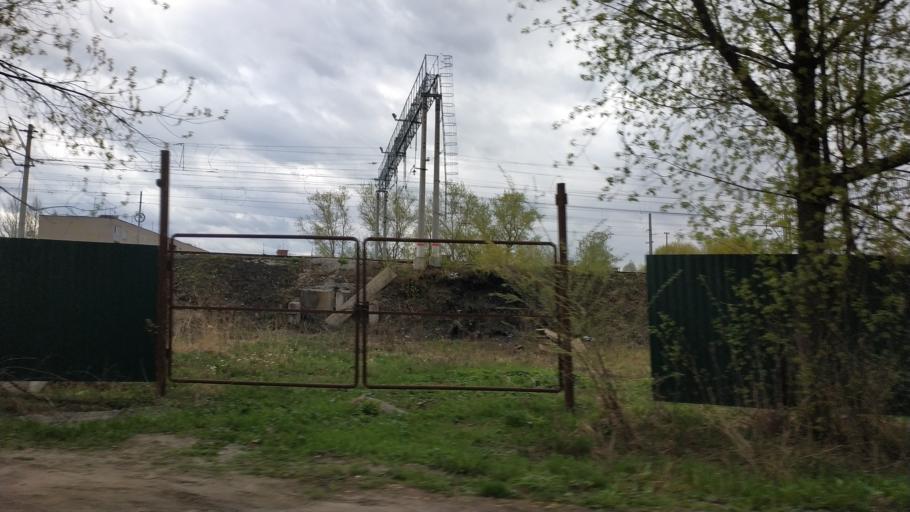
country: RU
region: Moskovskaya
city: Pavlovskiy Posad
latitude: 55.7756
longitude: 38.6852
